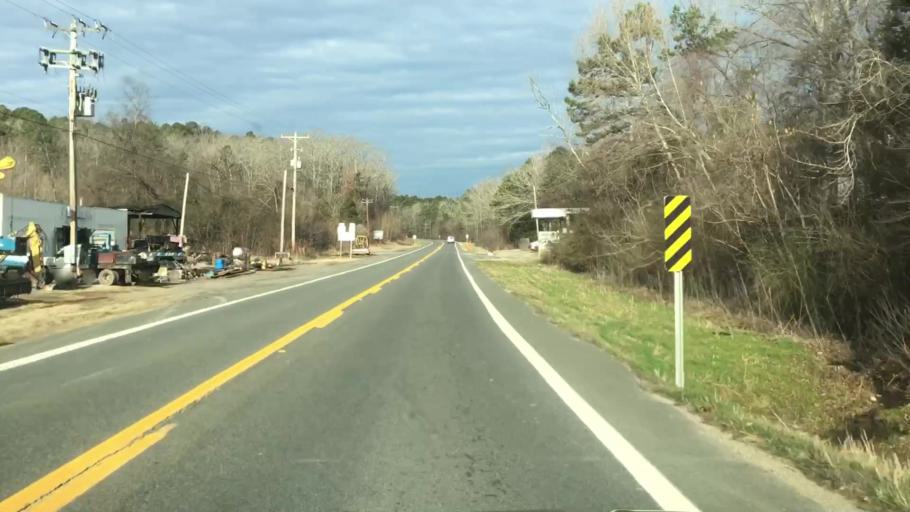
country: US
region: Arkansas
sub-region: Montgomery County
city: Mount Ida
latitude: 34.5632
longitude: -93.6413
